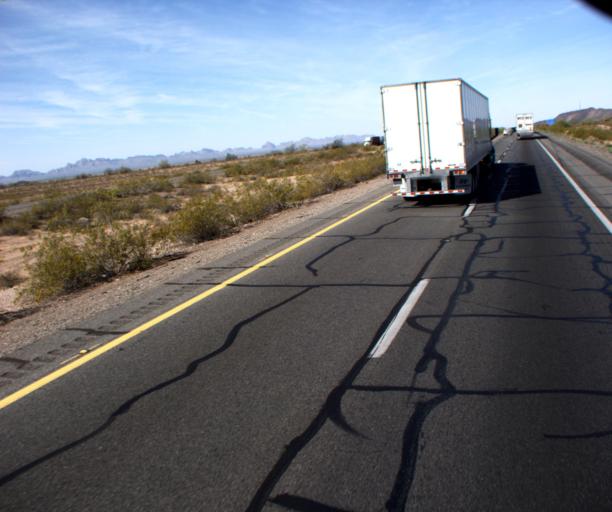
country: US
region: Arizona
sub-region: Maricopa County
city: Buckeye
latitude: 33.5178
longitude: -113.0517
